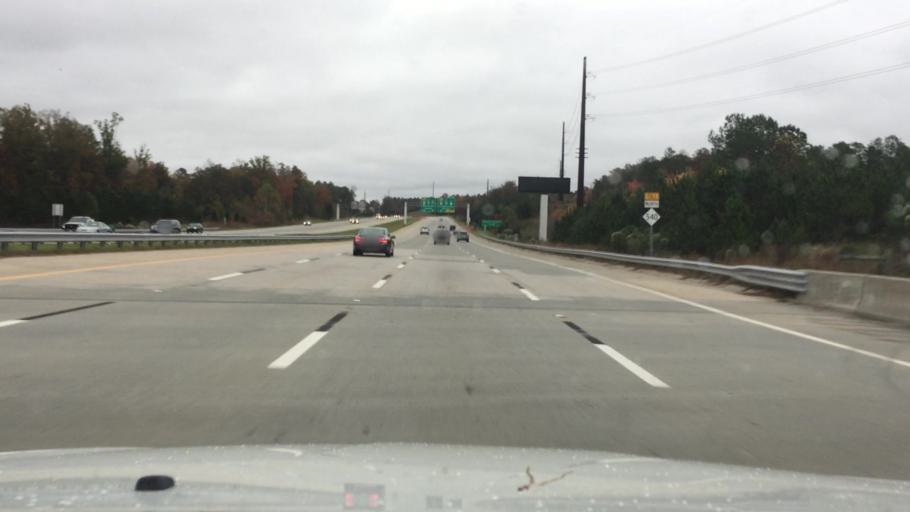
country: US
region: North Carolina
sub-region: Wake County
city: Morrisville
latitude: 35.8448
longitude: -78.8778
